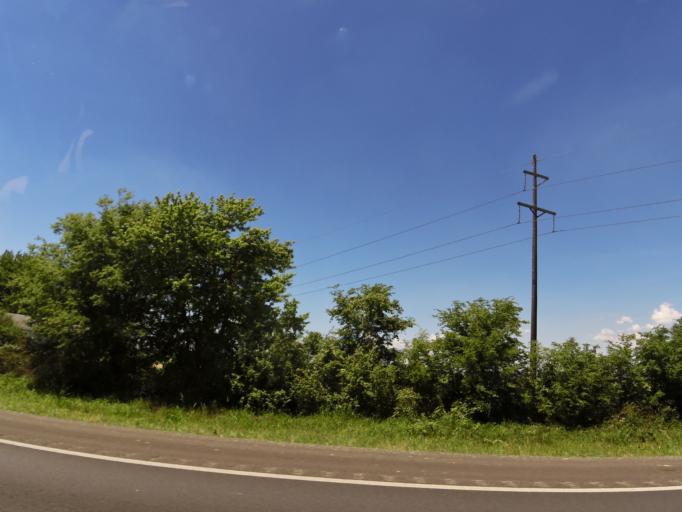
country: US
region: Missouri
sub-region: New Madrid County
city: Portageville
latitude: 36.4907
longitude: -89.6252
